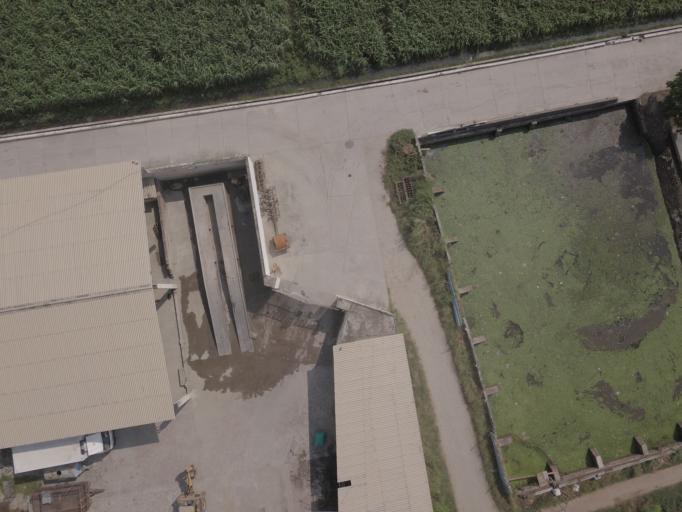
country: IN
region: Punjab
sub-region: Shahid Bhagat Singh Nagar
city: Rahon
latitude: 31.0189
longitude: 76.0929
